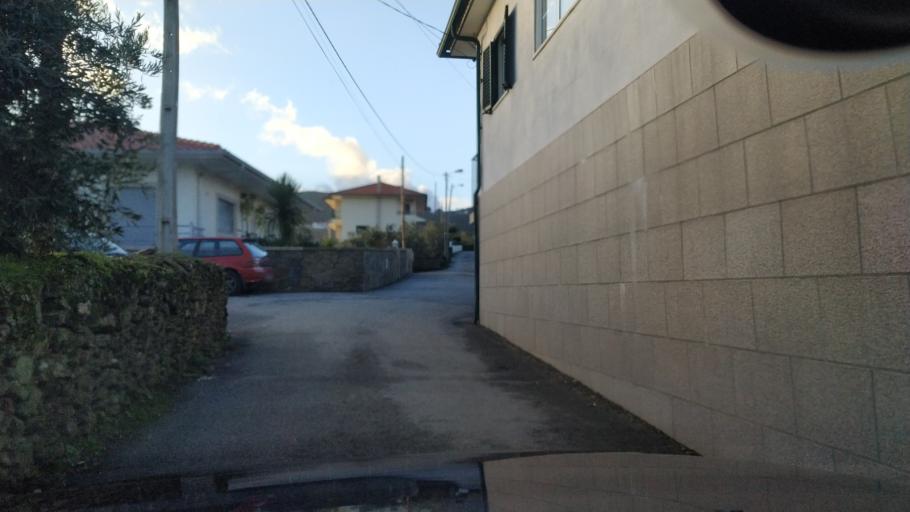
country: PT
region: Vila Real
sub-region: Vila Real
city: Vila Real
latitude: 41.2558
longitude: -7.7587
